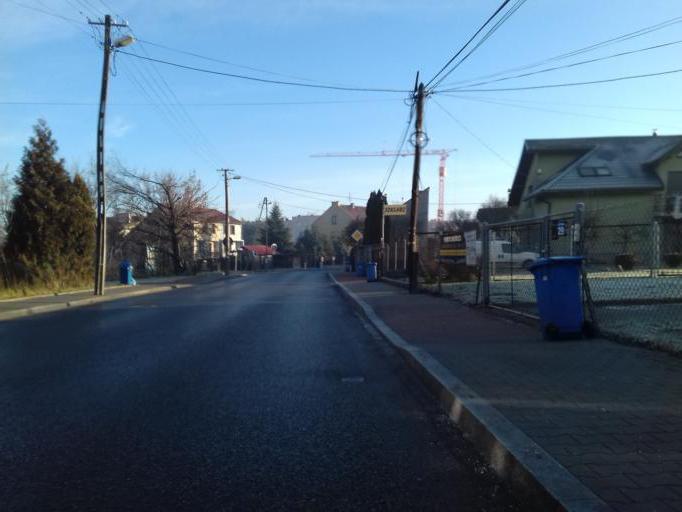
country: PL
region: Lesser Poland Voivodeship
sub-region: Krakow
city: Krakow
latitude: 50.0200
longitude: 19.9535
